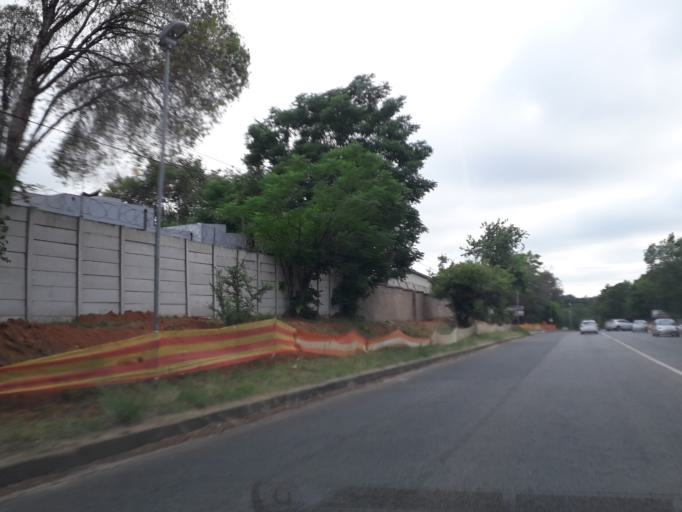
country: ZA
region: Gauteng
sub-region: City of Johannesburg Metropolitan Municipality
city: Roodepoort
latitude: -26.1030
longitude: 27.9482
